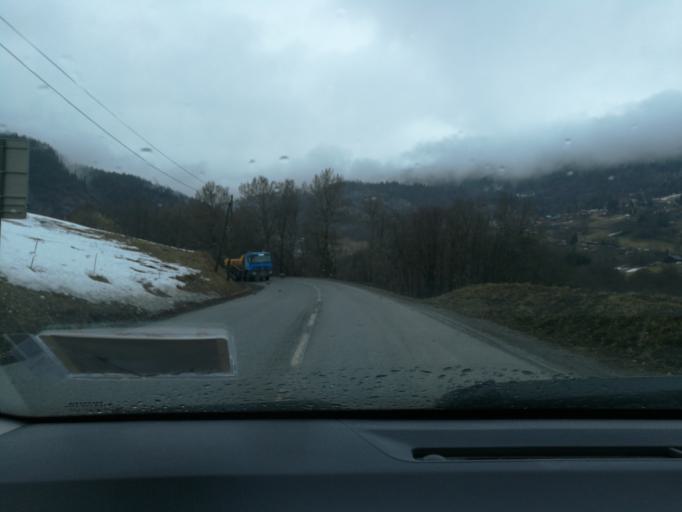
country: FR
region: Rhone-Alpes
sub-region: Departement de la Haute-Savoie
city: Araches-la-Frasse
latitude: 46.0446
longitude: 6.6250
